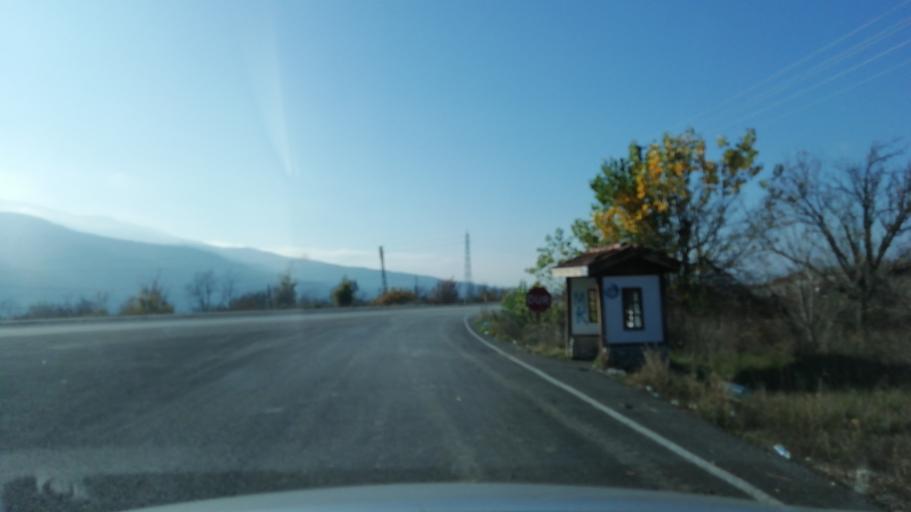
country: TR
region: Karabuk
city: Safranbolu
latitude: 41.2236
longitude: 32.7769
